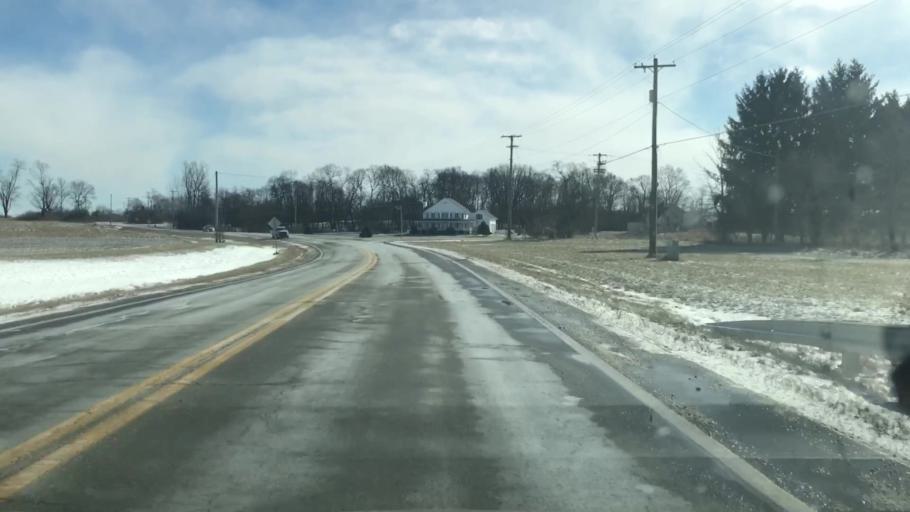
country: US
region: Ohio
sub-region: Madison County
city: Plain City
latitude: 40.0401
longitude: -83.2515
